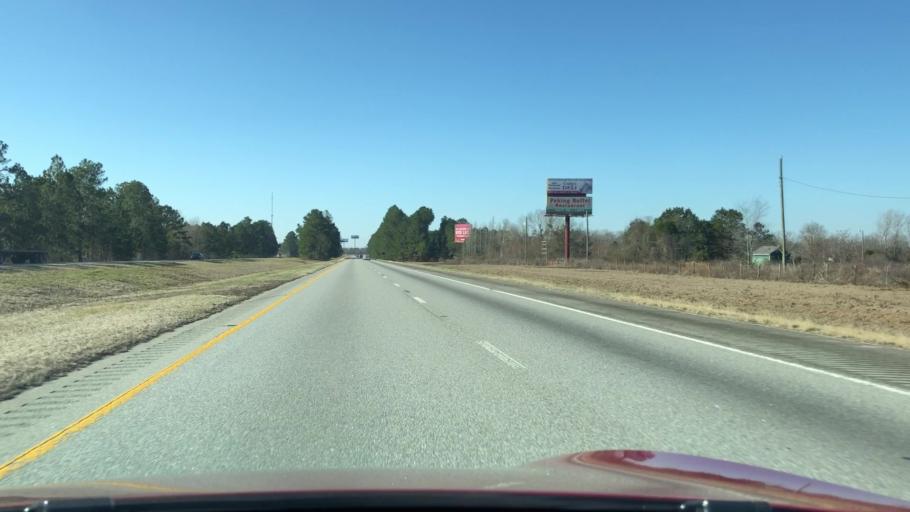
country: US
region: South Carolina
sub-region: Clarendon County
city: Manning
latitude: 33.6087
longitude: -80.3186
